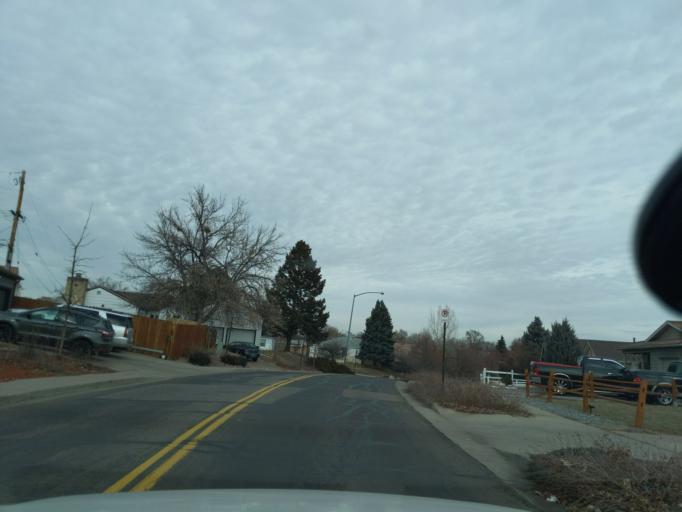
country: US
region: Colorado
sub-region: Adams County
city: Thornton
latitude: 39.8603
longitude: -104.9591
